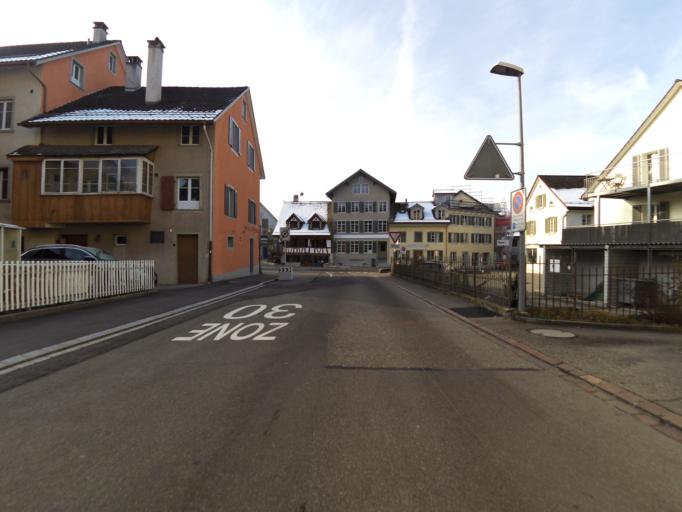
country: CH
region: Thurgau
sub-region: Frauenfeld District
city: Frauenfeld
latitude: 47.5551
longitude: 8.9006
